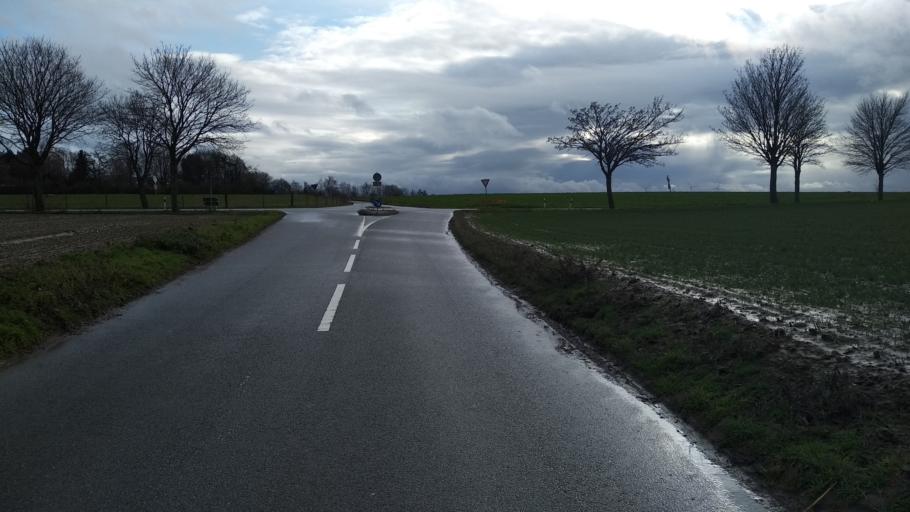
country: DE
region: North Rhine-Westphalia
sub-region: Regierungsbezirk Dusseldorf
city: Korschenbroich
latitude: 51.1405
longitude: 6.5443
